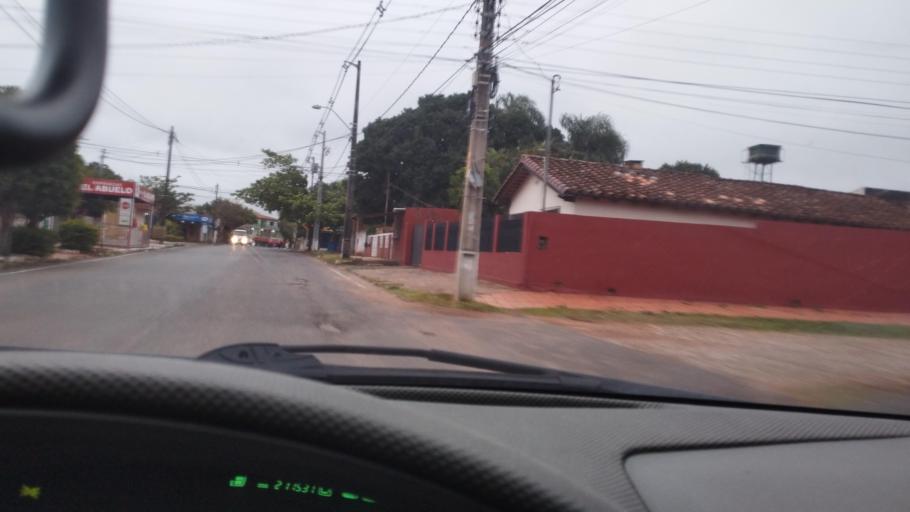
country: PY
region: Central
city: Fernando de la Mora
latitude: -25.3027
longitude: -57.5304
